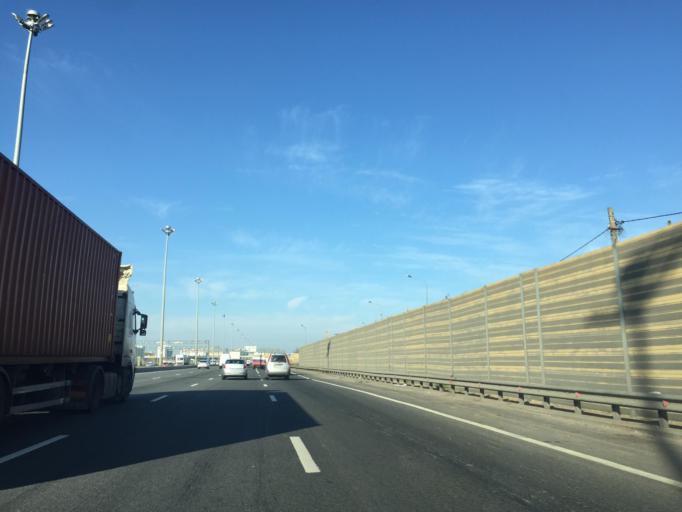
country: RU
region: St.-Petersburg
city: Petro-Slavyanka
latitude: 59.7479
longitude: 30.4990
